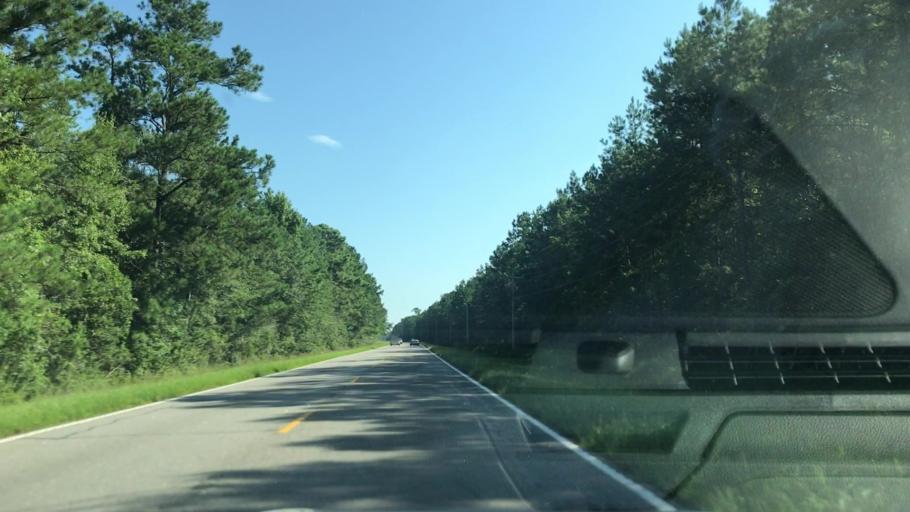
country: US
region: South Carolina
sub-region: Georgetown County
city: Georgetown
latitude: 33.5042
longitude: -79.2561
